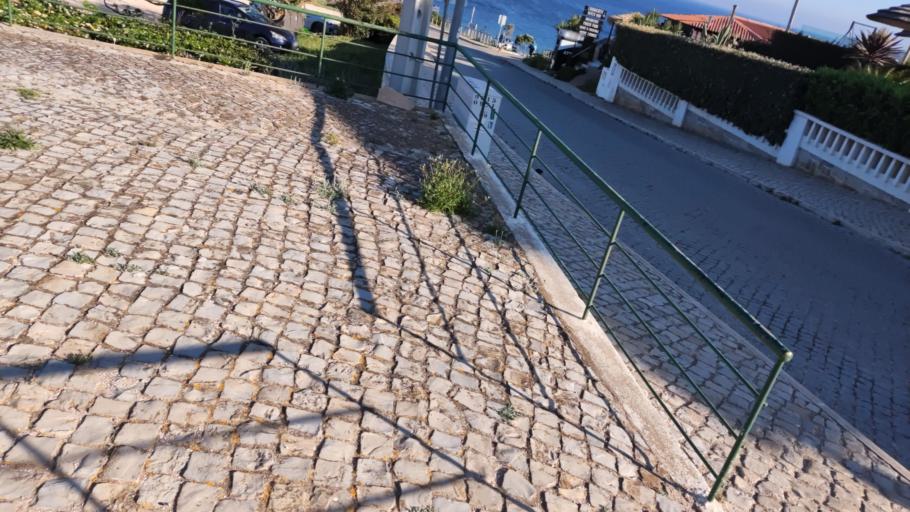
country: PT
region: Faro
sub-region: Vila do Bispo
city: Sagres
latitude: 37.0069
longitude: -8.9412
